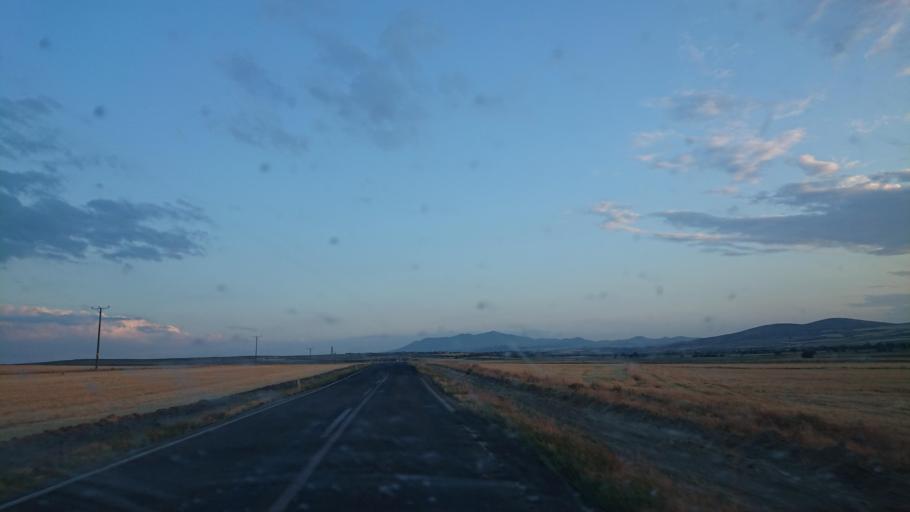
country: TR
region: Aksaray
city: Balci
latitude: 38.8203
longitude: 34.1353
